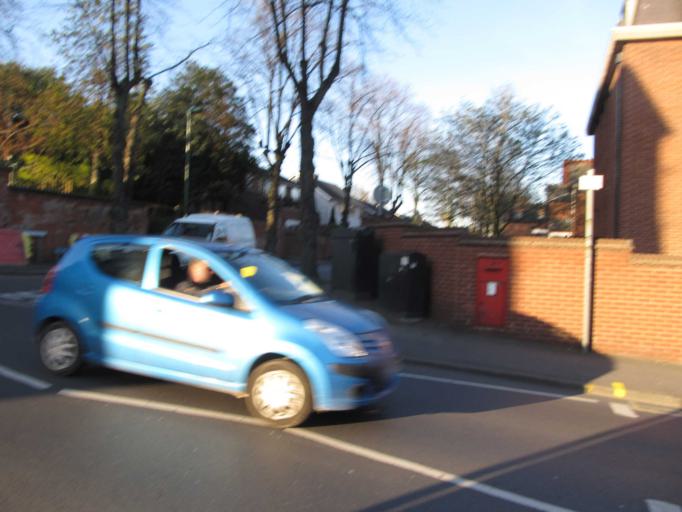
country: GB
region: England
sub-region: Nottingham
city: Nottingham
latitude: 52.9711
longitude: -1.1585
